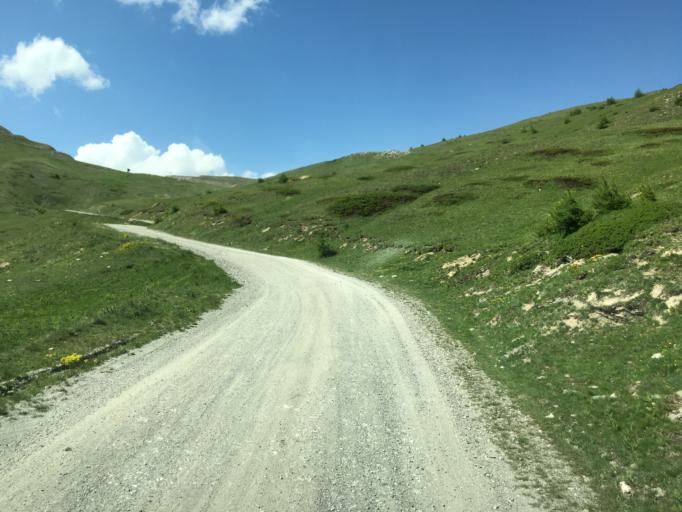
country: IT
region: Piedmont
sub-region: Provincia di Torino
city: Sestriere
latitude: 44.9820
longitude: 6.8721
